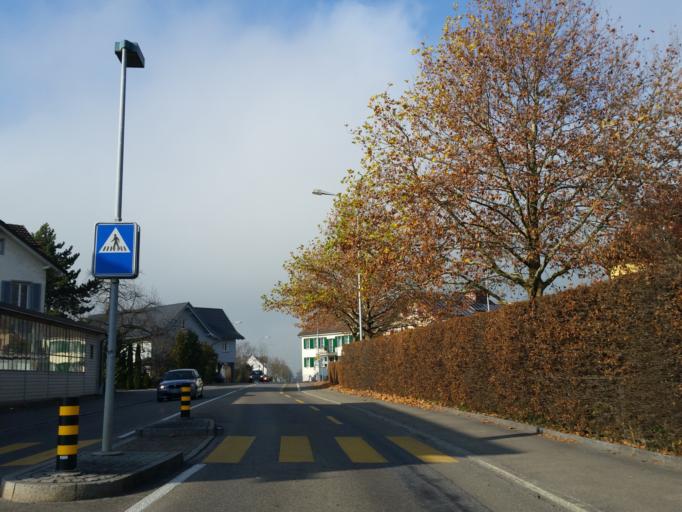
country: CH
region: Thurgau
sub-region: Arbon District
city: Roggwil
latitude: 47.5276
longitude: 9.4057
